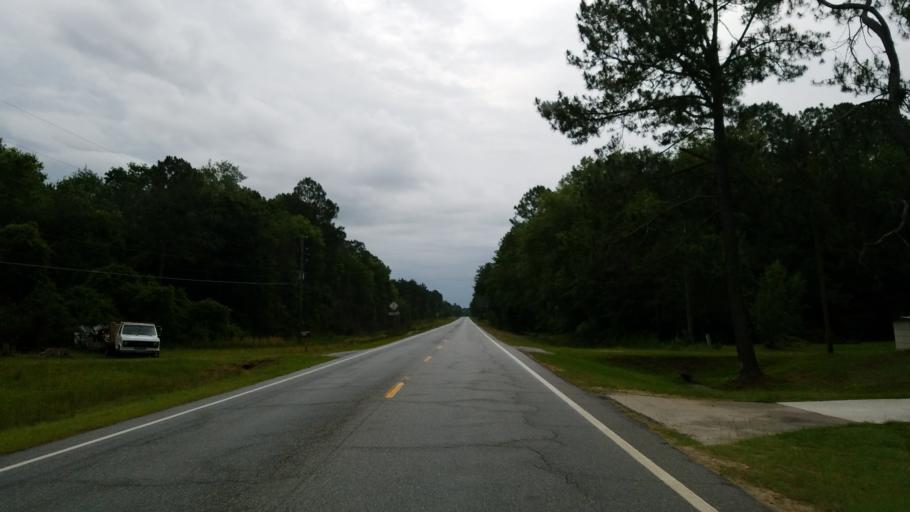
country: US
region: Georgia
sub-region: Berrien County
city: Ray City
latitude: 31.0807
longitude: -83.2268
